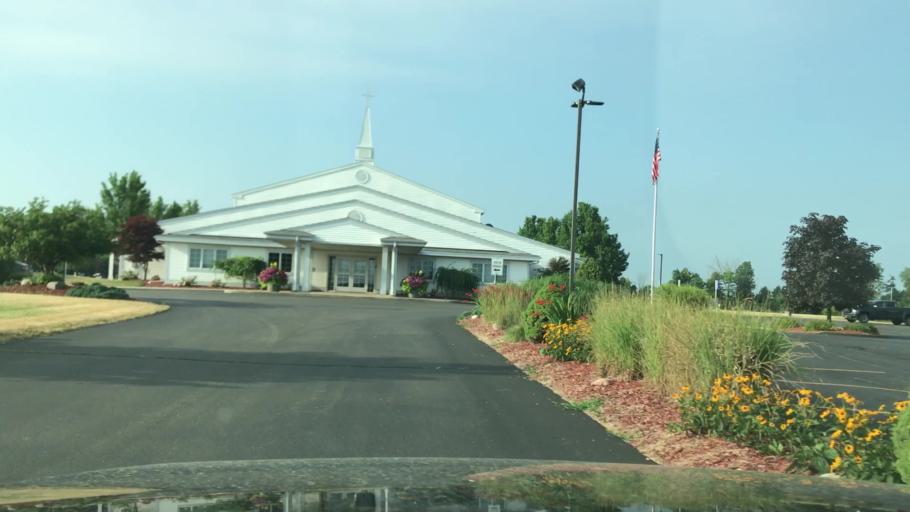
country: US
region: Michigan
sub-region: Ottawa County
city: Hudsonville
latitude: 42.8393
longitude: -85.8438
